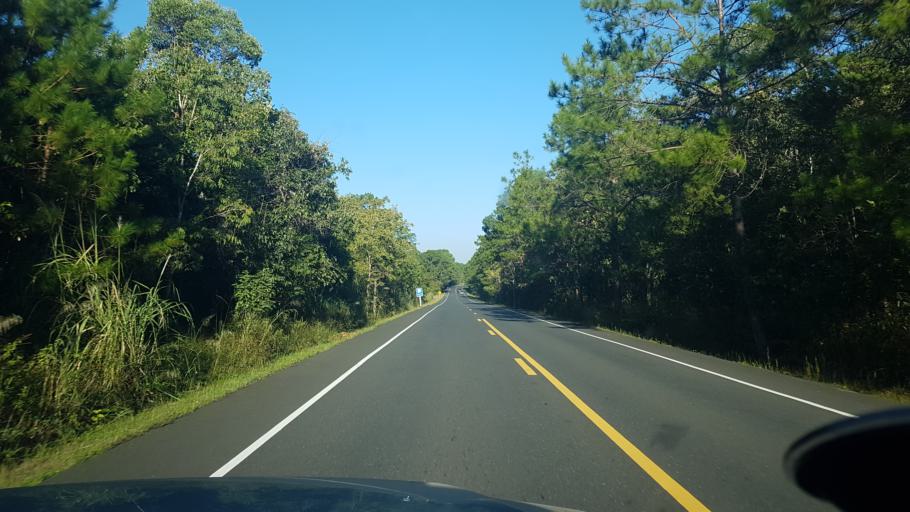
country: TH
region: Phetchabun
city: Nam Nao
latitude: 16.7187
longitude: 101.5923
